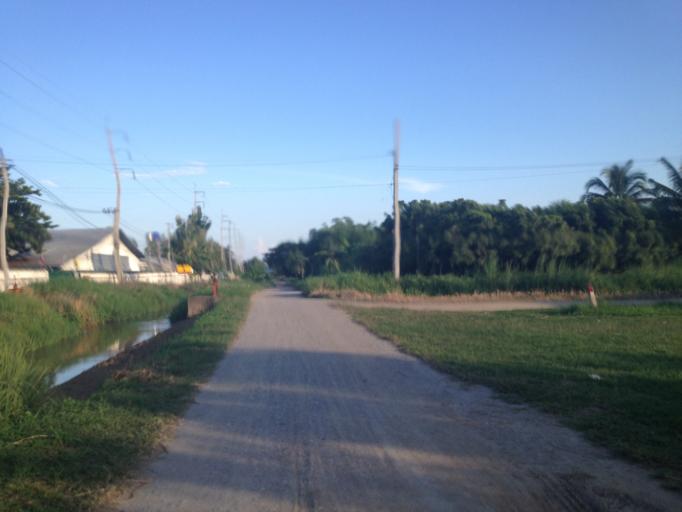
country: TH
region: Chiang Mai
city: Hang Dong
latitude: 18.6794
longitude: 98.8986
